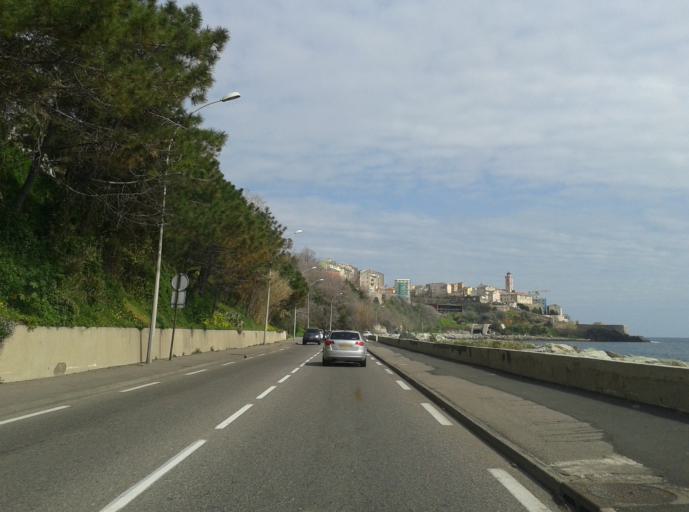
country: FR
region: Corsica
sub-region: Departement de la Haute-Corse
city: Bastia
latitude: 42.6871
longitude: 9.4465
